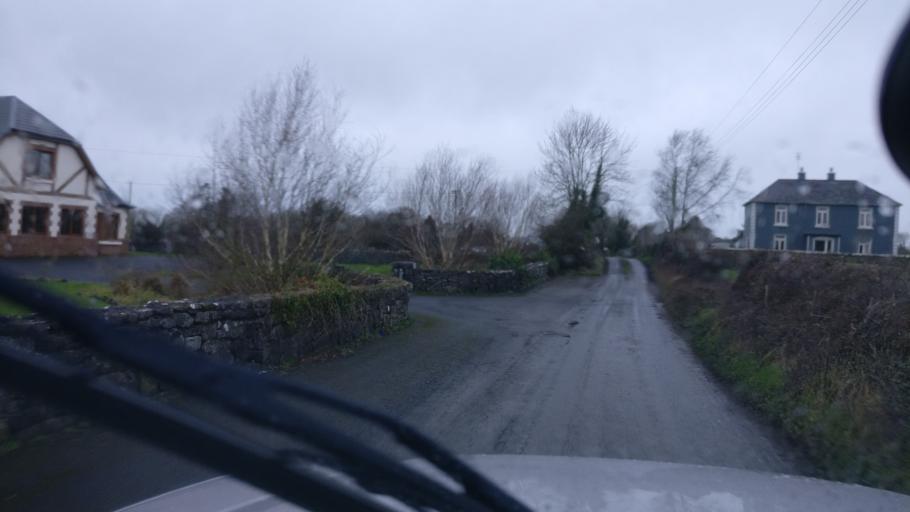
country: IE
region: Connaught
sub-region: County Galway
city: Loughrea
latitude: 53.1876
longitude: -8.6131
